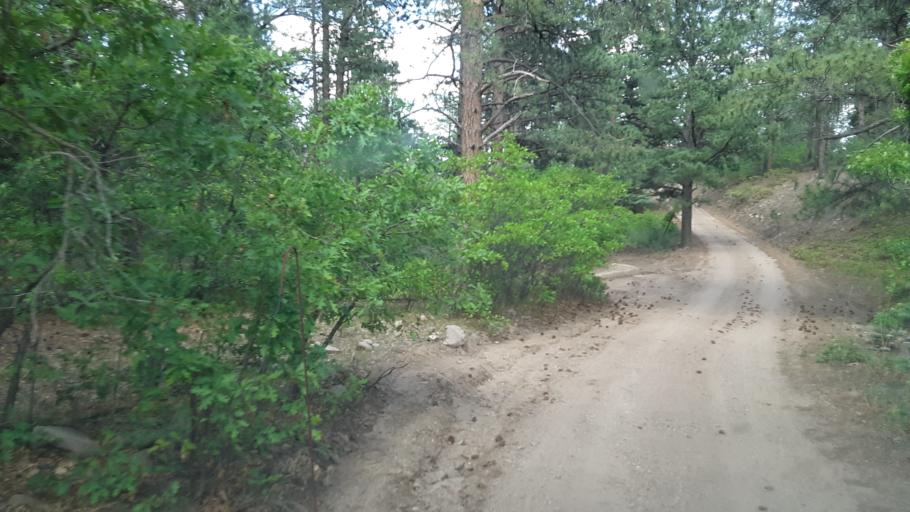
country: US
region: Colorado
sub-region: Custer County
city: Westcliffe
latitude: 38.2219
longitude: -105.6182
